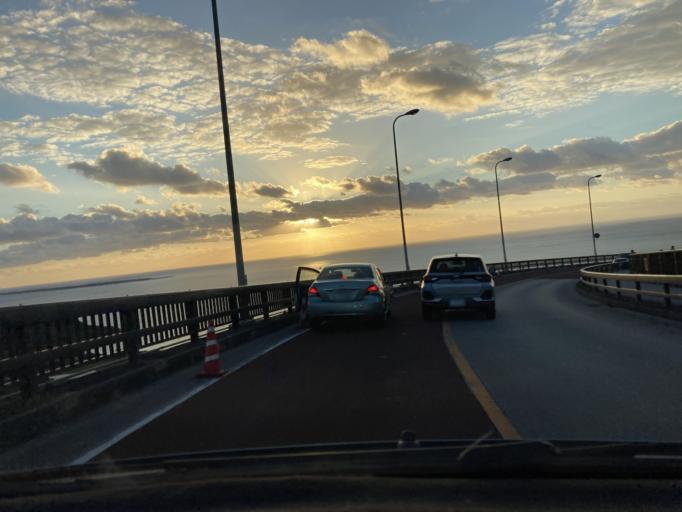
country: JP
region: Okinawa
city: Ginowan
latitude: 26.1673
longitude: 127.8156
